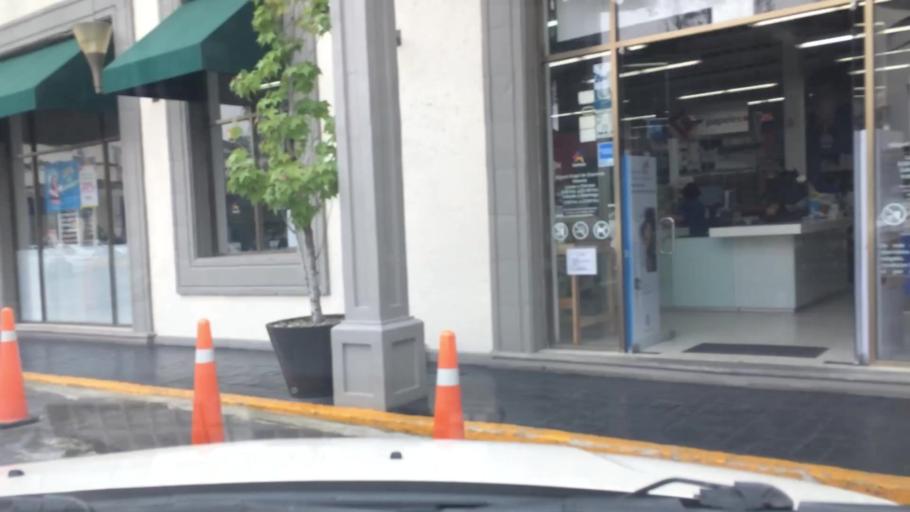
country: MX
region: Mexico City
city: Coyoacan
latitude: 19.3454
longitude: -99.1774
